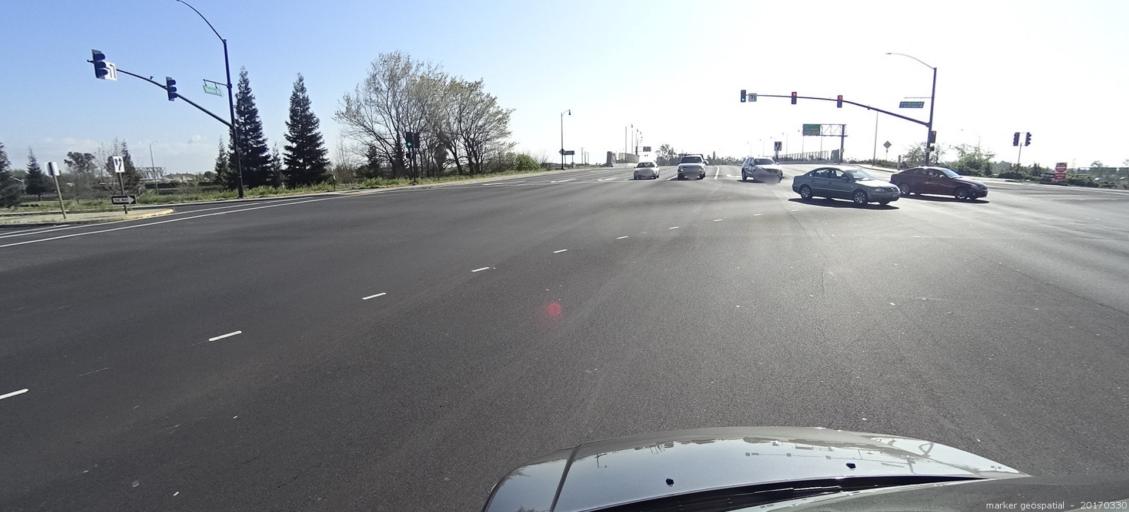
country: US
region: California
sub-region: Sacramento County
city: Laguna
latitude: 38.4379
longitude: -121.4037
